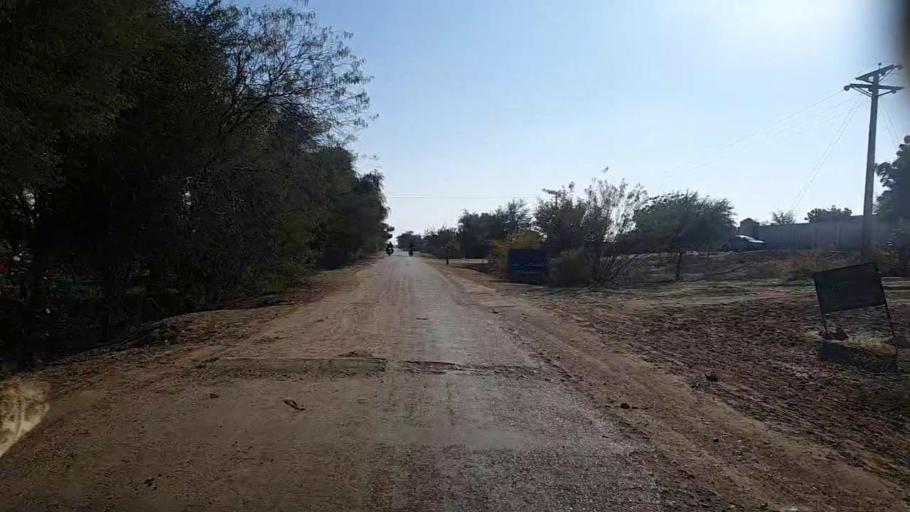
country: PK
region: Sindh
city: Khairpur
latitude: 27.9108
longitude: 69.7510
